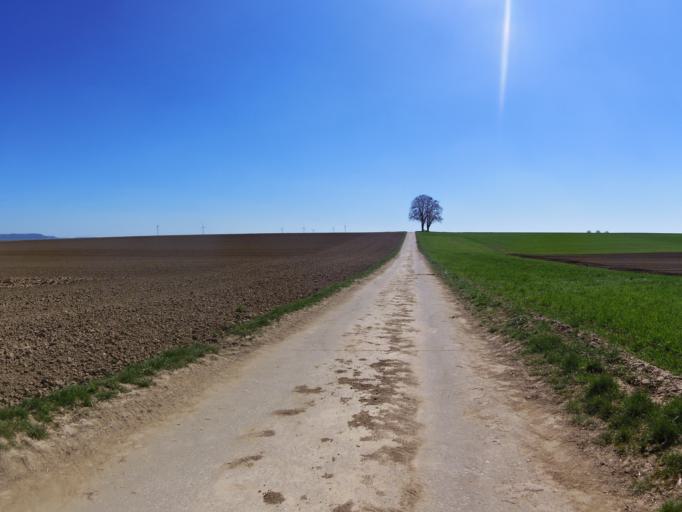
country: DE
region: Bavaria
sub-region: Regierungsbezirk Unterfranken
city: Biebelried
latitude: 49.8138
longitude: 10.0867
